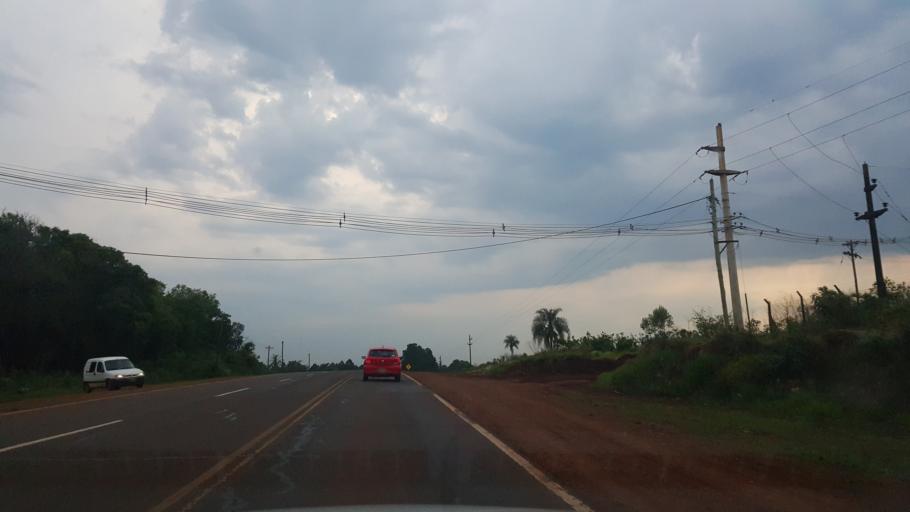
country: AR
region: Misiones
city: Santo Pipo
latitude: -27.1303
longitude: -55.3904
